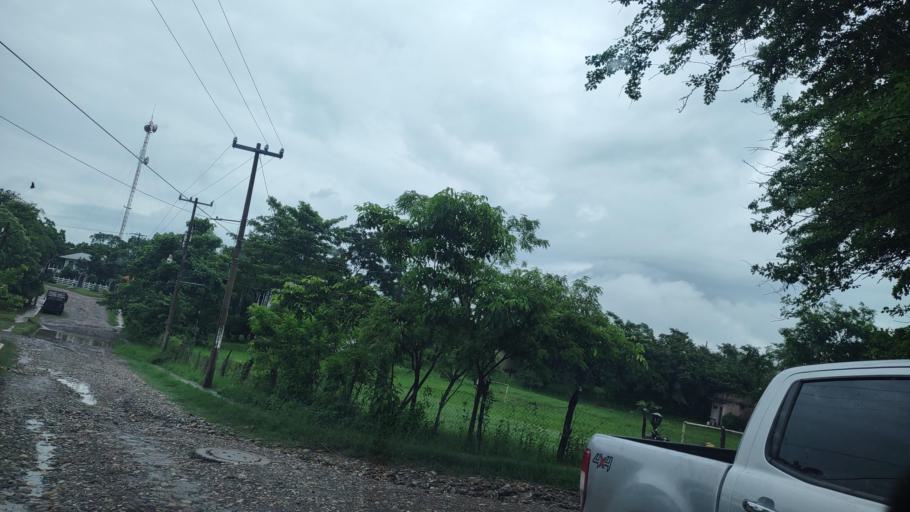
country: MX
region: San Luis Potosi
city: Tanquian de Escobedo
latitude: 21.5446
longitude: -98.5523
